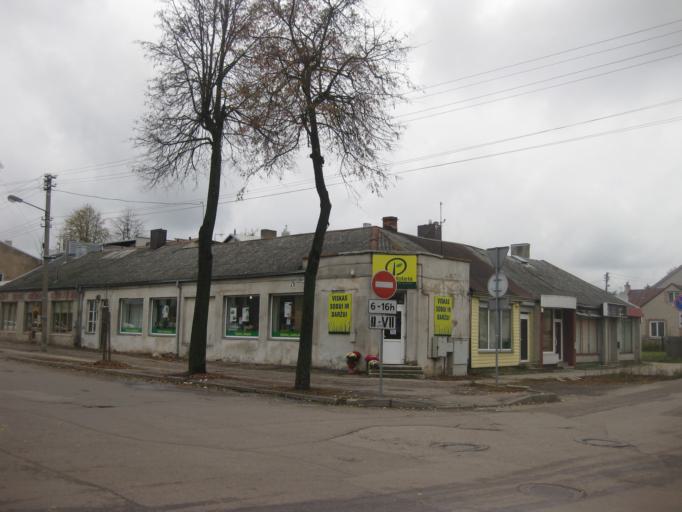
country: LT
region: Kauno apskritis
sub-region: Kaunas
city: Kaunas
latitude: 54.9077
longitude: 23.9181
